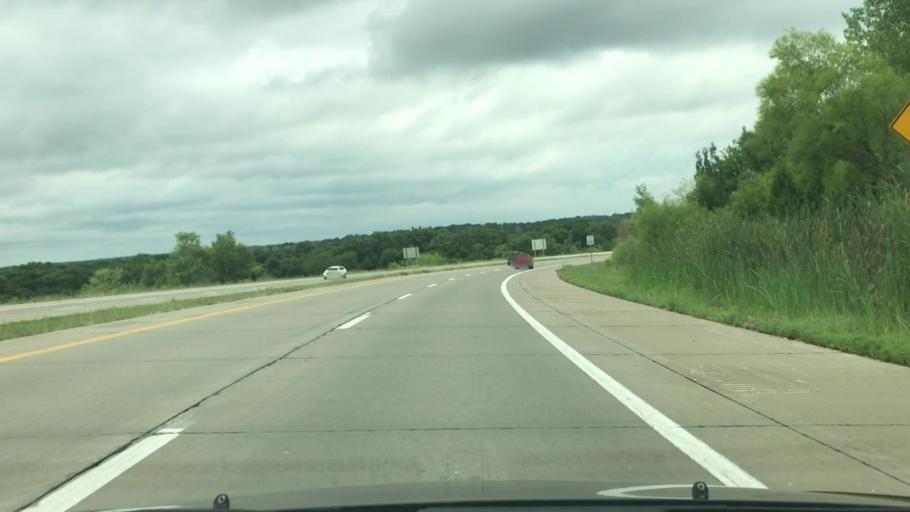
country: US
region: Missouri
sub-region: Jackson County
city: Grandview
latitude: 38.8637
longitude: -94.5963
